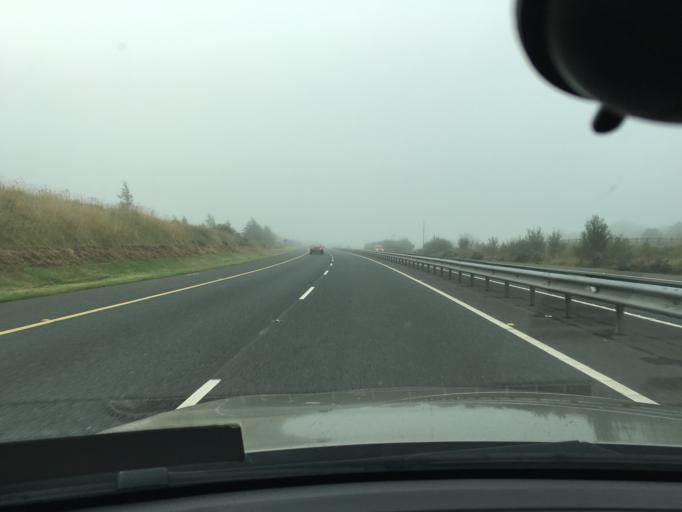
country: IE
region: Leinster
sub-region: An Iarmhi
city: Athlone
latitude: 53.3608
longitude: -8.0632
